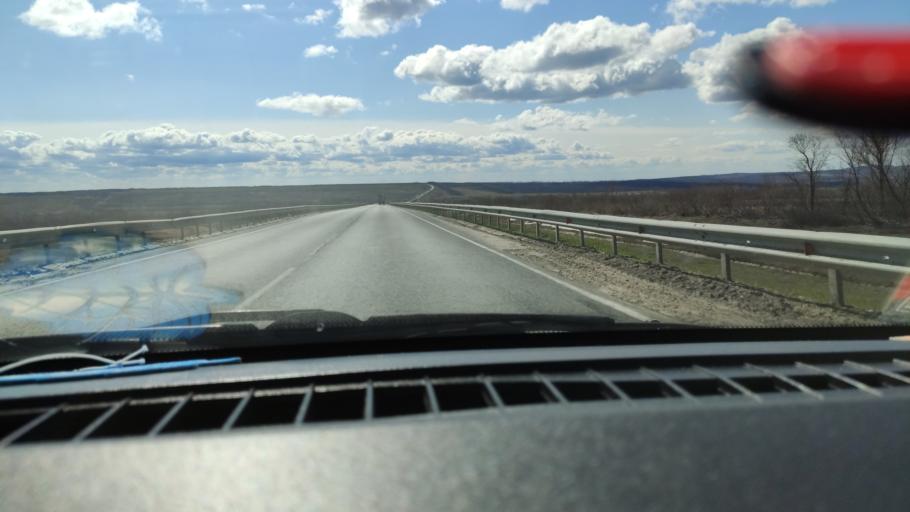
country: RU
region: Saratov
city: Dukhovnitskoye
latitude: 52.7521
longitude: 48.2474
